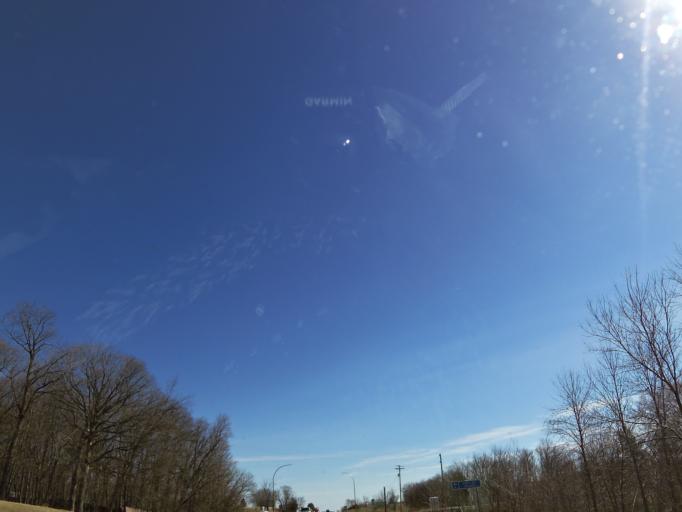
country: US
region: Minnesota
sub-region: Wright County
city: Buffalo
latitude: 45.1457
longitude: -93.8381
